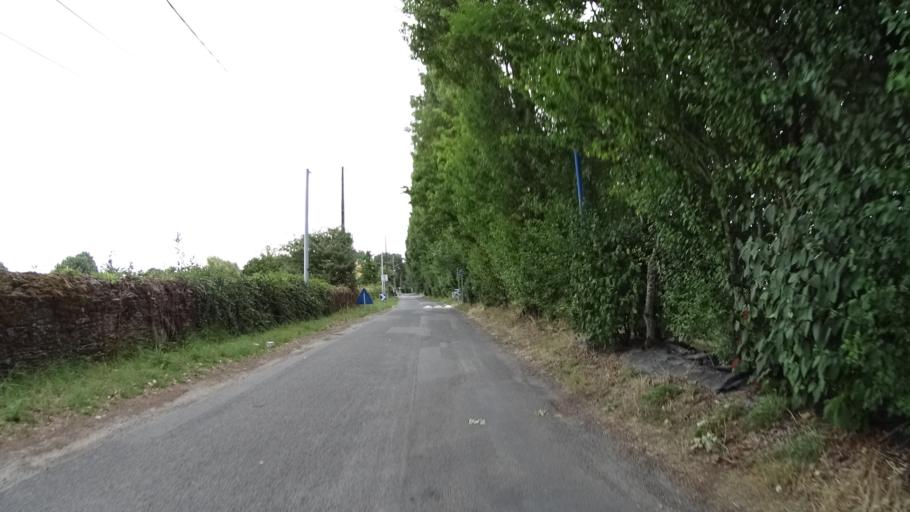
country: FR
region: Pays de la Loire
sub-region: Departement de la Loire-Atlantique
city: Sainte-Luce-sur-Loire
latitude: 47.2412
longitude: -1.4665
